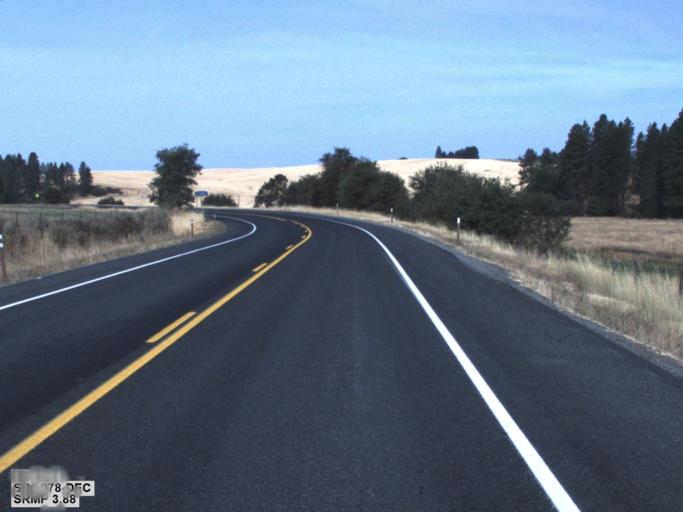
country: US
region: Idaho
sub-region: Benewah County
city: Plummer
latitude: 47.4435
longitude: -117.0714
